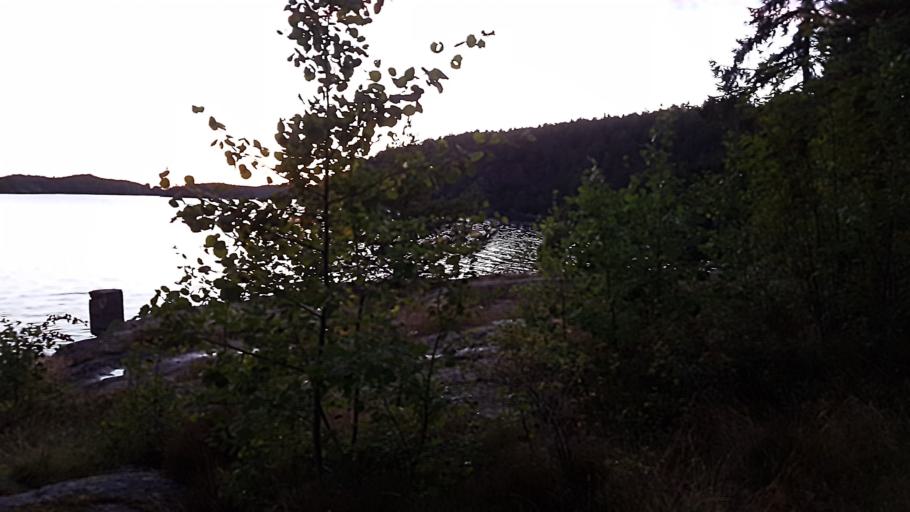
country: SE
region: Soedermanland
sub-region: Nykopings Kommun
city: Svalsta
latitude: 58.6124
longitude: 16.9041
